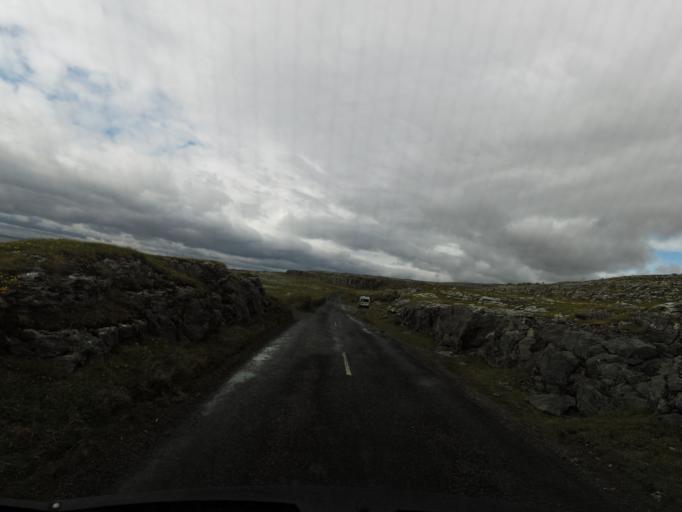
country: IE
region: Connaught
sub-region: County Galway
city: Bearna
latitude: 53.0626
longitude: -9.3612
